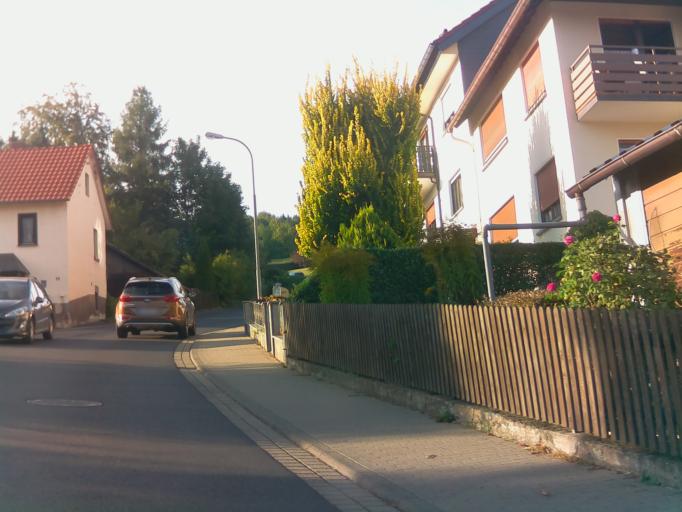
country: DE
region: Hesse
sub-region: Regierungsbezirk Darmstadt
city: Bad Soden-Salmunster
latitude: 50.3217
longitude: 9.3722
